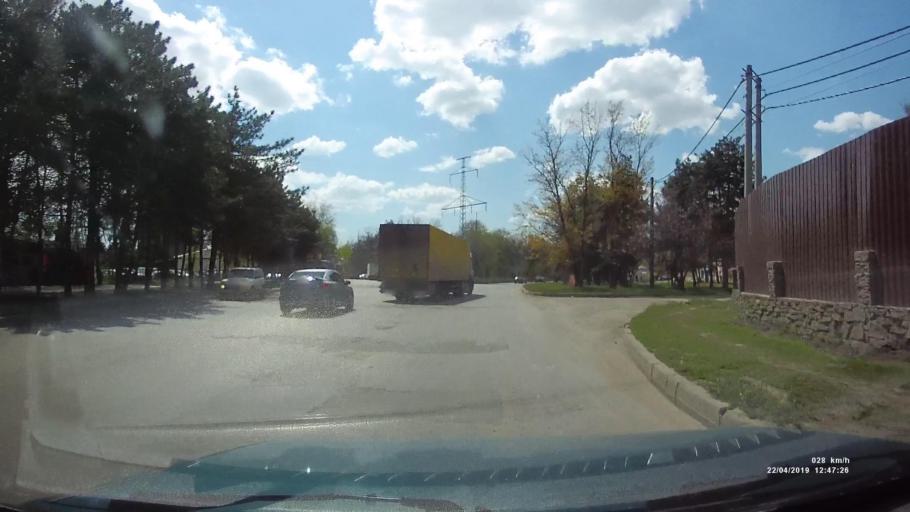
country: RU
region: Rostov
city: Azov
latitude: 47.0986
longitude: 39.4103
